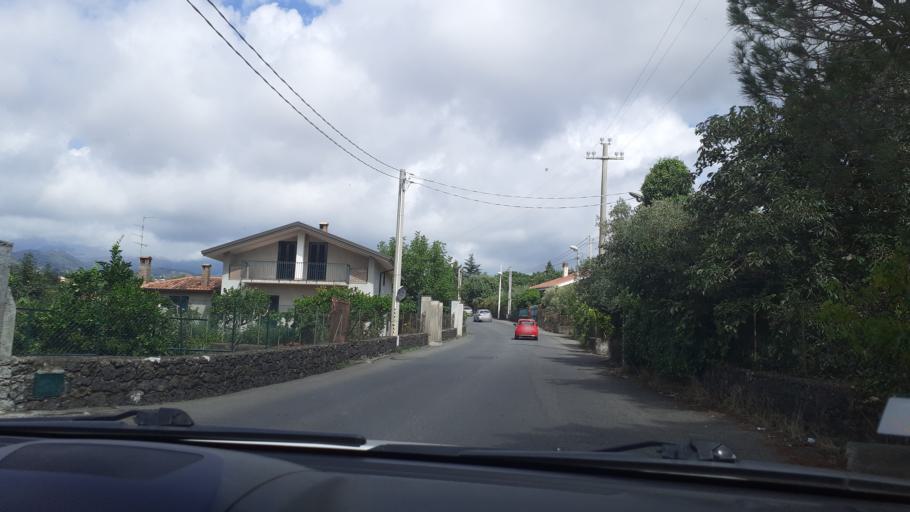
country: IT
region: Sicily
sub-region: Catania
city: Trecastagni
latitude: 37.6013
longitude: 15.0727
